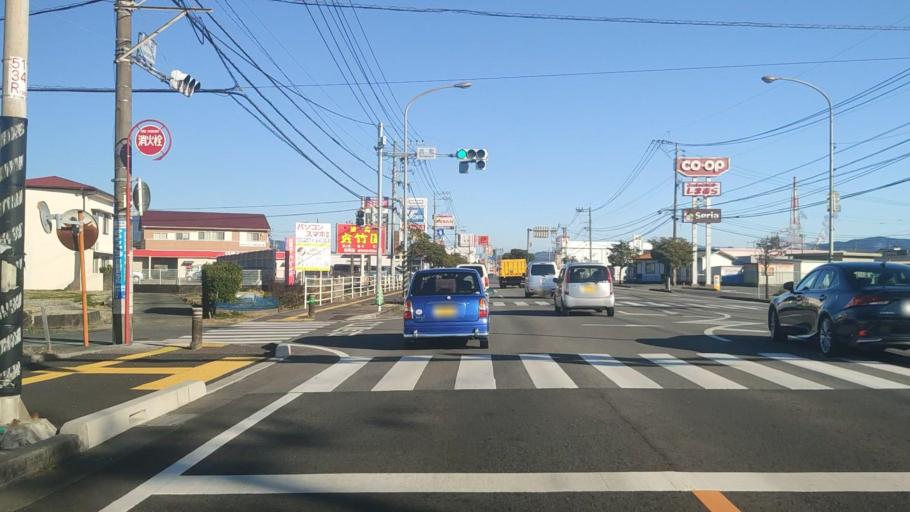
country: JP
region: Miyazaki
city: Nobeoka
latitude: 32.5585
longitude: 131.6802
